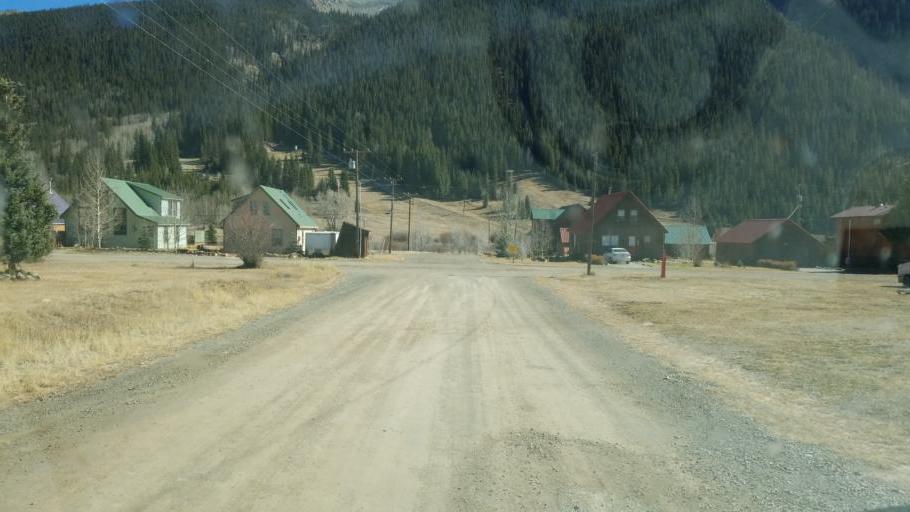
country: US
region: Colorado
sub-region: San Juan County
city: Silverton
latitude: 37.8137
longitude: -107.6591
